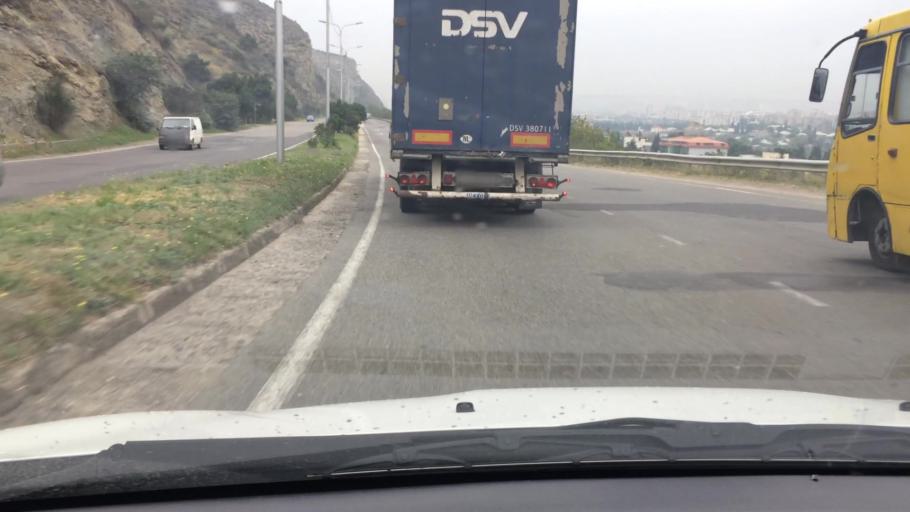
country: GE
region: T'bilisi
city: Tbilisi
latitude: 41.6518
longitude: 44.9043
